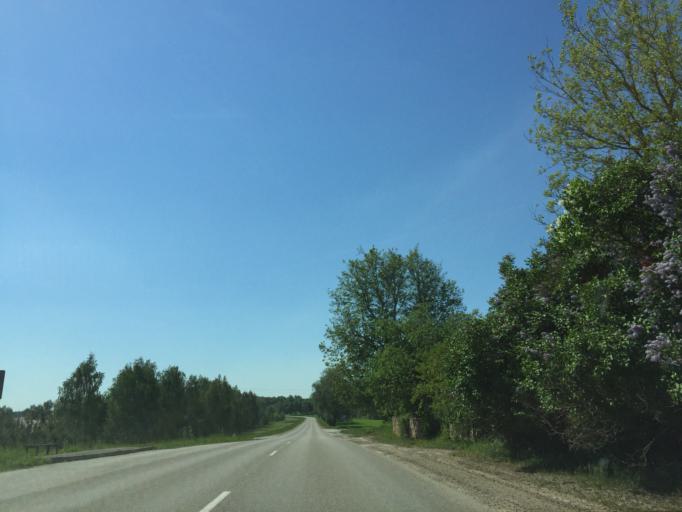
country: LV
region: Bauskas Rajons
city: Bauska
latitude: 56.4268
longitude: 24.2862
